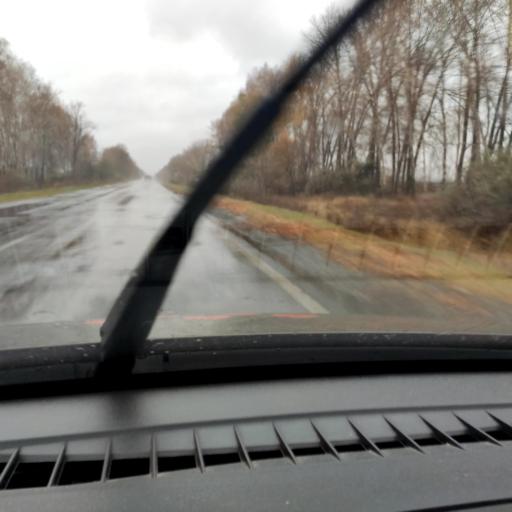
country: RU
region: Samara
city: Tol'yatti
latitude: 53.6600
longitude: 49.2857
